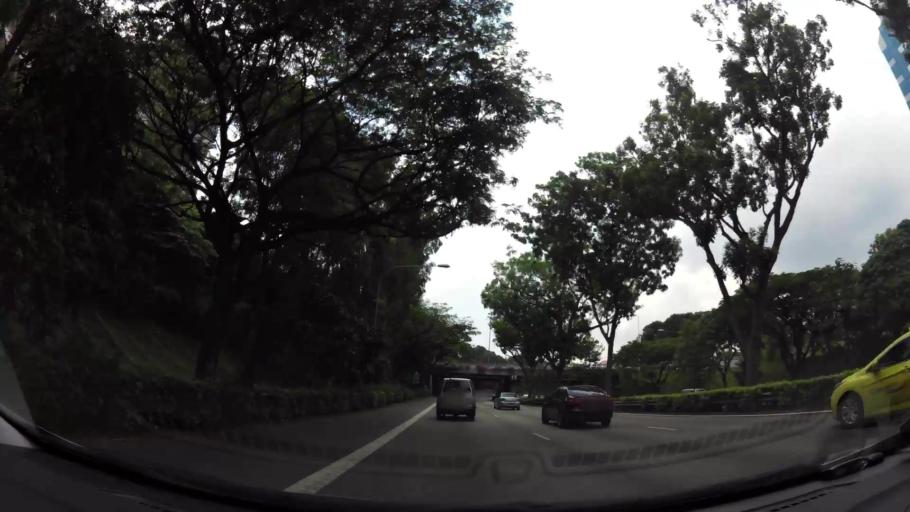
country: SG
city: Singapore
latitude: 1.2839
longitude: 103.8024
